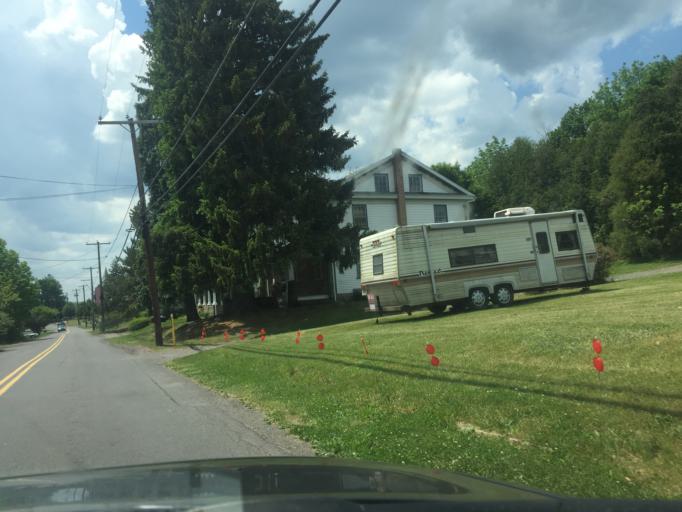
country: US
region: Pennsylvania
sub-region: Luzerne County
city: Harleigh
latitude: 41.0287
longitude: -76.0048
